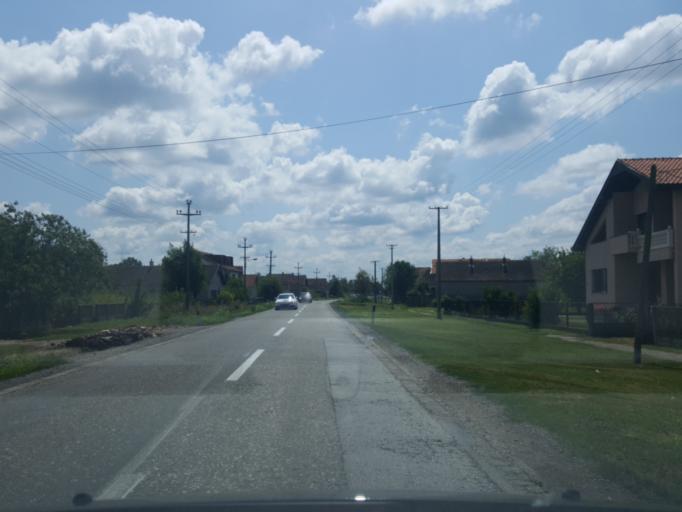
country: RS
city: Metkovic
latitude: 44.8594
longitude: 19.5454
